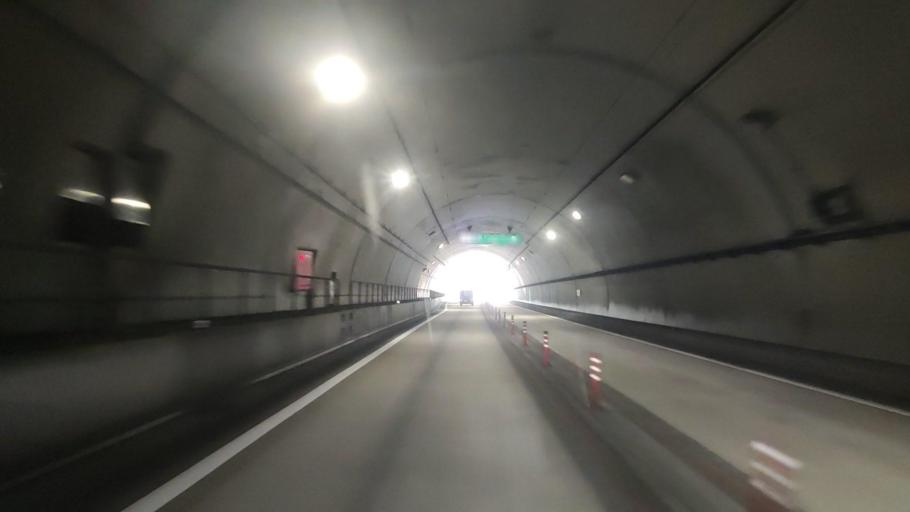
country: JP
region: Wakayama
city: Tanabe
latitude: 33.5527
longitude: 135.5125
